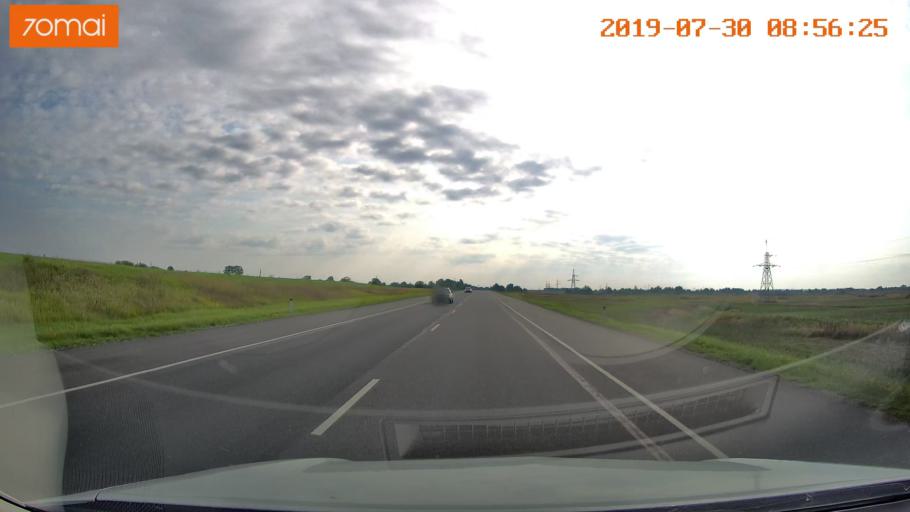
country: RU
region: Kaliningrad
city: Gusev
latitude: 54.5993
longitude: 22.0770
